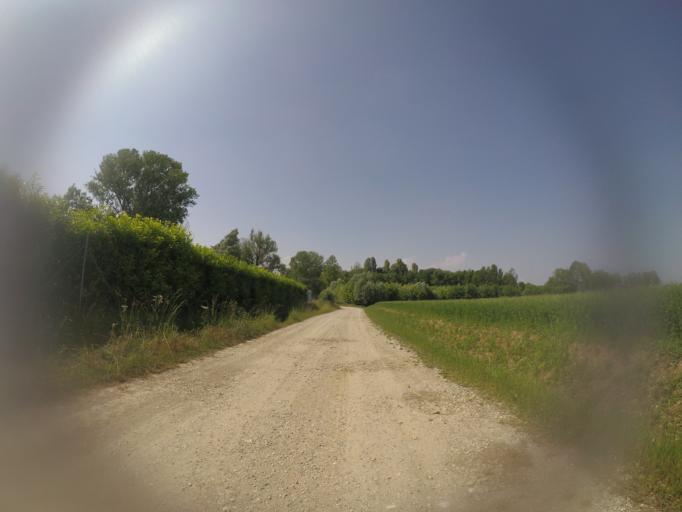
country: IT
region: Friuli Venezia Giulia
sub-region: Provincia di Udine
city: Bertiolo
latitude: 45.9383
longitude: 13.0271
